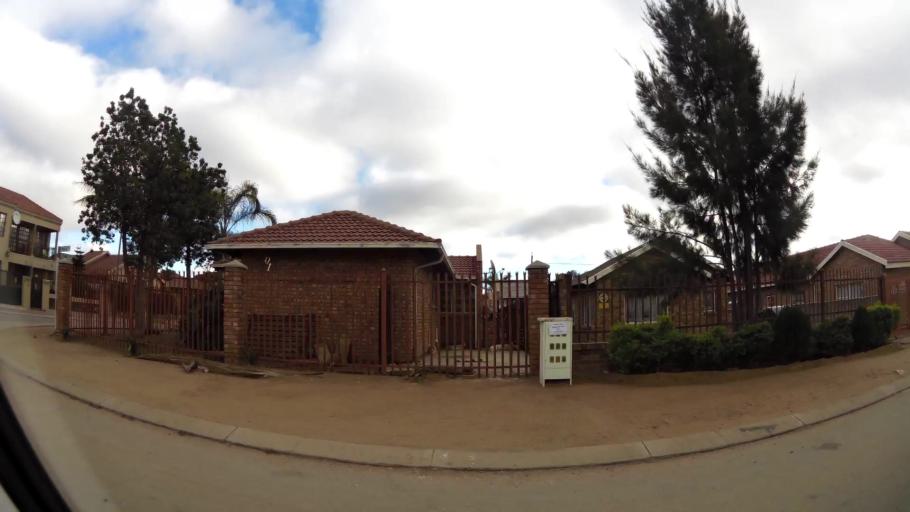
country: ZA
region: Limpopo
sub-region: Capricorn District Municipality
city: Polokwane
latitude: -23.9264
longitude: 29.4449
